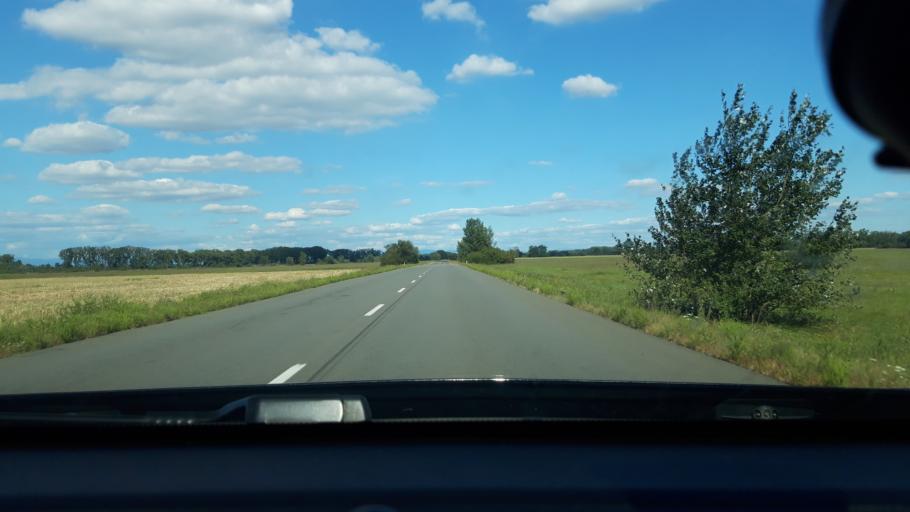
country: SK
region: Kosicky
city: Trebisov
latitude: 48.5235
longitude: 21.8448
